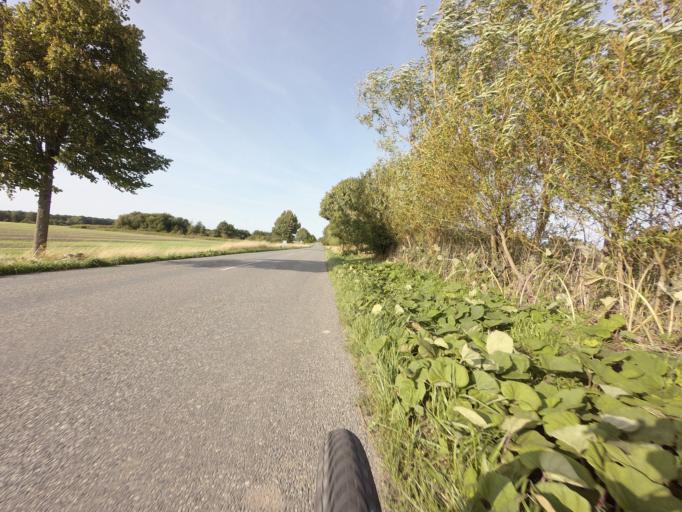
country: DK
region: Zealand
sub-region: Faxe Kommune
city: Fakse Ladeplads
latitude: 55.2389
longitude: 12.2154
